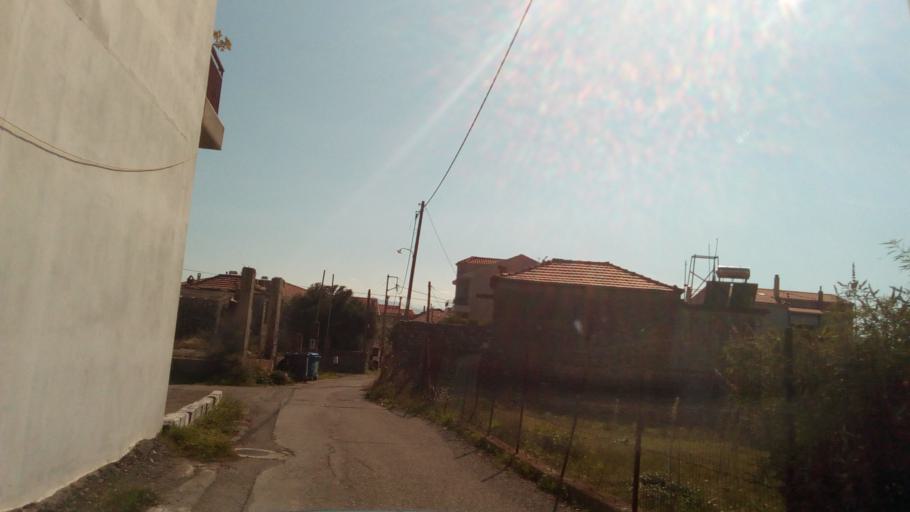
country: GR
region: West Greece
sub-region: Nomos Aitolias kai Akarnanias
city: Nafpaktos
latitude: 38.3977
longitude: 21.8446
